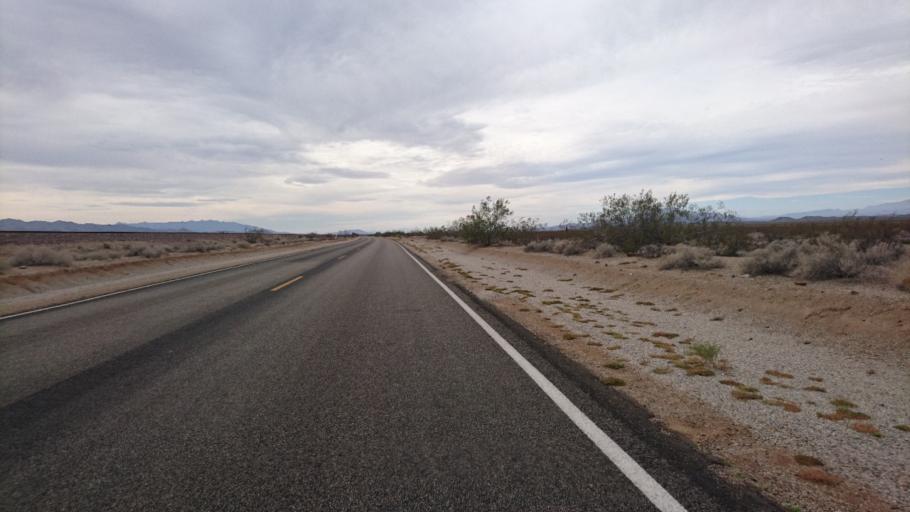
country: US
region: California
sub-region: San Bernardino County
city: Needles
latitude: 34.8737
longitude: -115.1106
